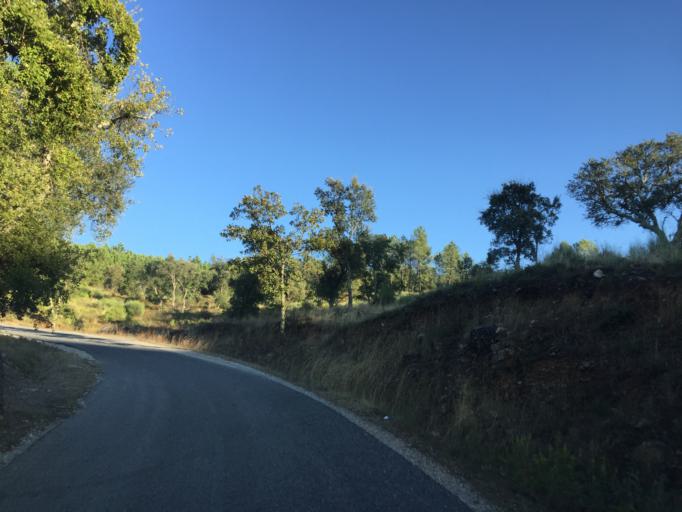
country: PT
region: Portalegre
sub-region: Castelo de Vide
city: Castelo de Vide
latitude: 39.4015
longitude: -7.4493
